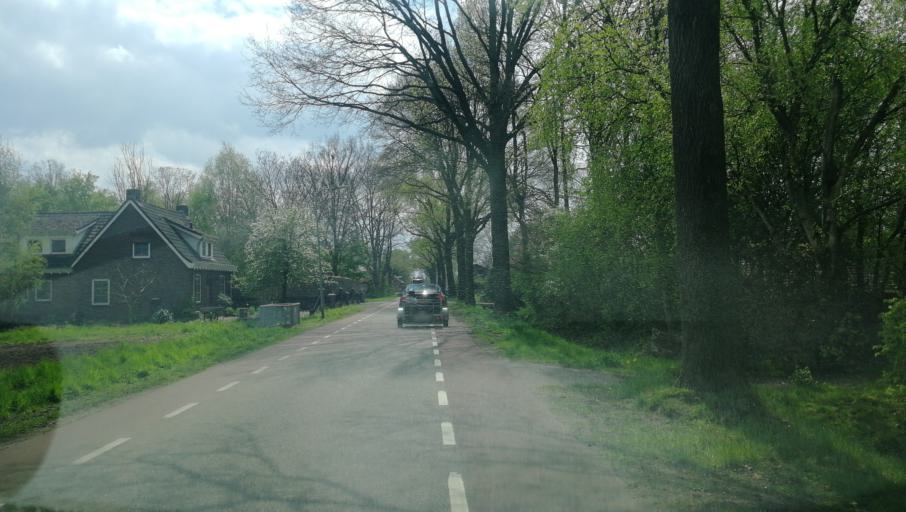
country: NL
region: Limburg
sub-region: Gemeente Peel en Maas
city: Maasbree
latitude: 51.4349
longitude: 6.0284
